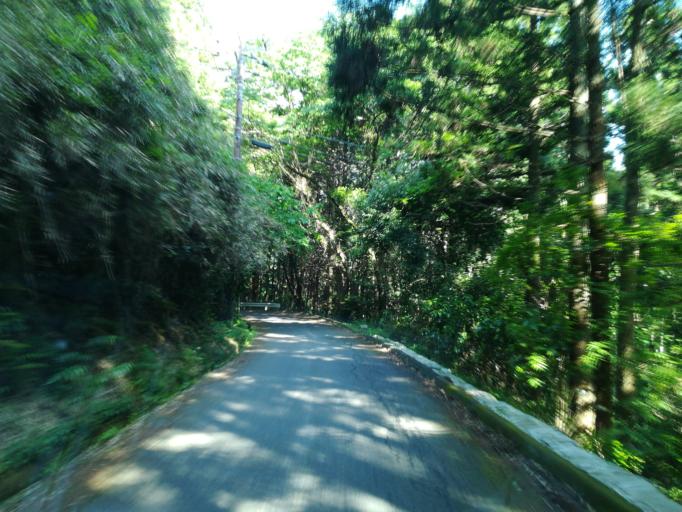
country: JP
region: Ibaraki
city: Tsukuba
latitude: 36.1867
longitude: 140.1392
